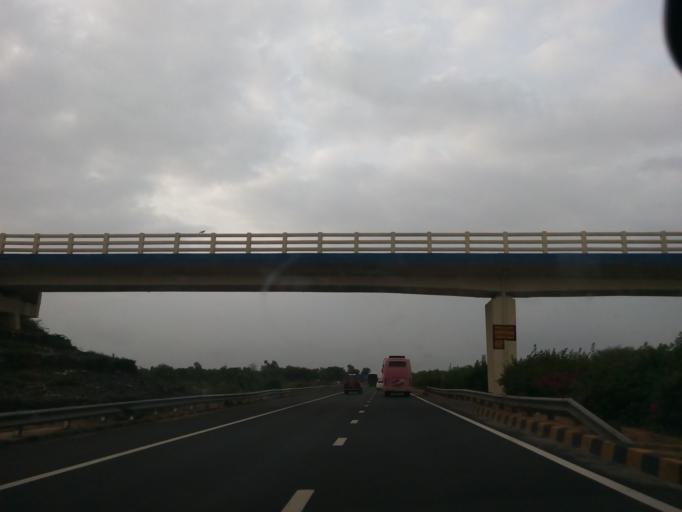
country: IN
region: Gujarat
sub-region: Kheda
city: Mahemdavad
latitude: 22.8934
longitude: 72.7829
